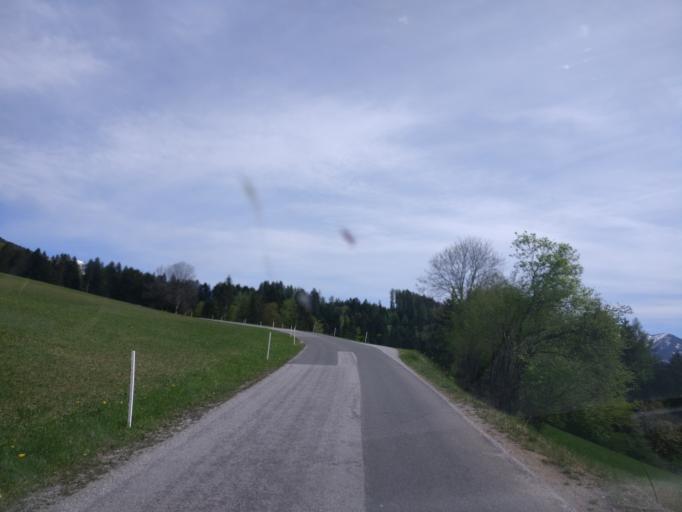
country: AT
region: Salzburg
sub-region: Politischer Bezirk Sankt Johann im Pongau
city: Pfarrwerfen
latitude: 47.4717
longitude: 13.2055
